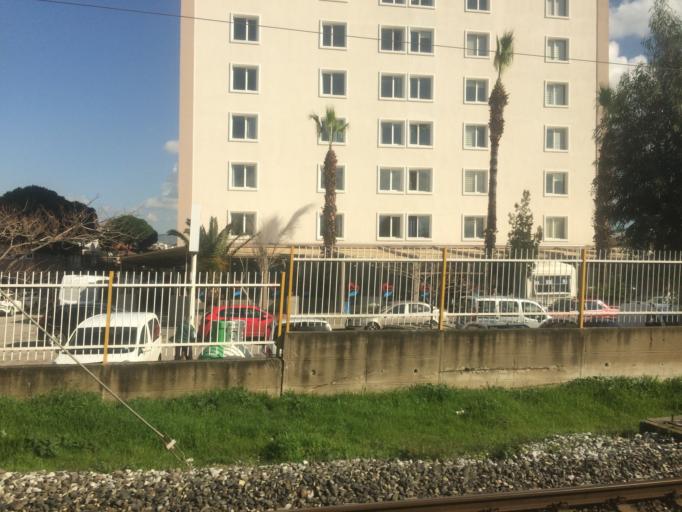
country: TR
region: Izmir
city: Karsiyaka
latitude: 38.4611
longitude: 27.1664
